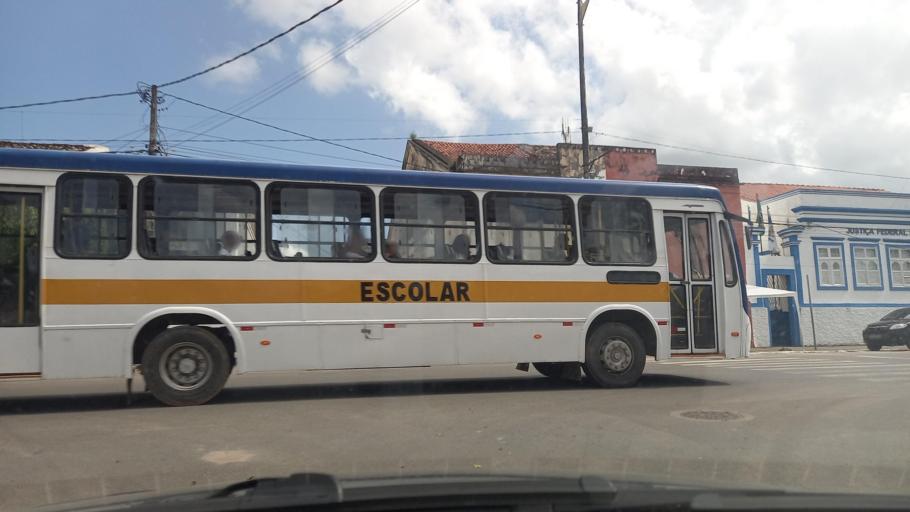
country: BR
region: Pernambuco
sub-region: Goiana
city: Goiana
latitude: -7.5574
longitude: -34.9998
